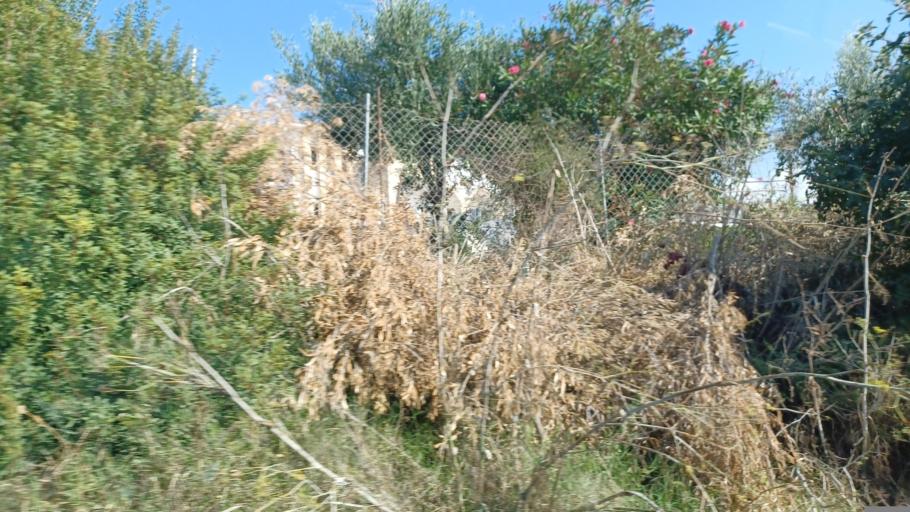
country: CY
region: Pafos
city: Kissonerga
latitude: 34.8452
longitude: 32.3936
